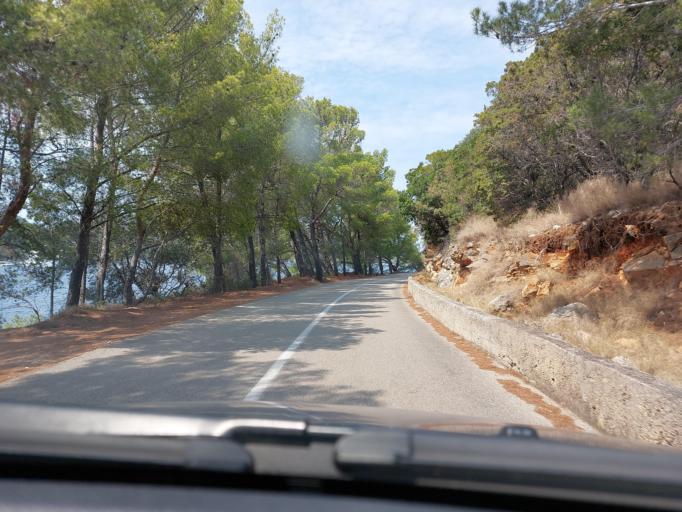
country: HR
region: Dubrovacko-Neretvanska
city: Smokvica
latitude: 42.7578
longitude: 16.8232
